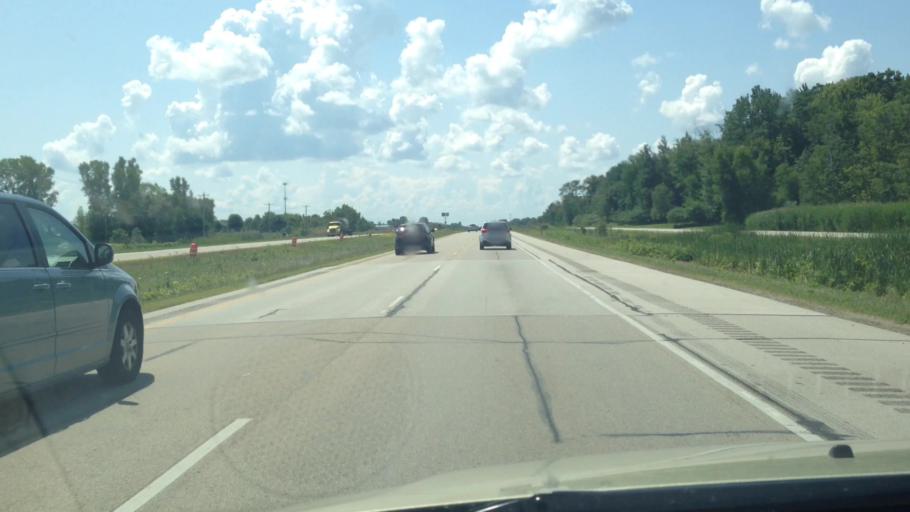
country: US
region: Wisconsin
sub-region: Brown County
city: Suamico
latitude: 44.6934
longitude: -88.0508
